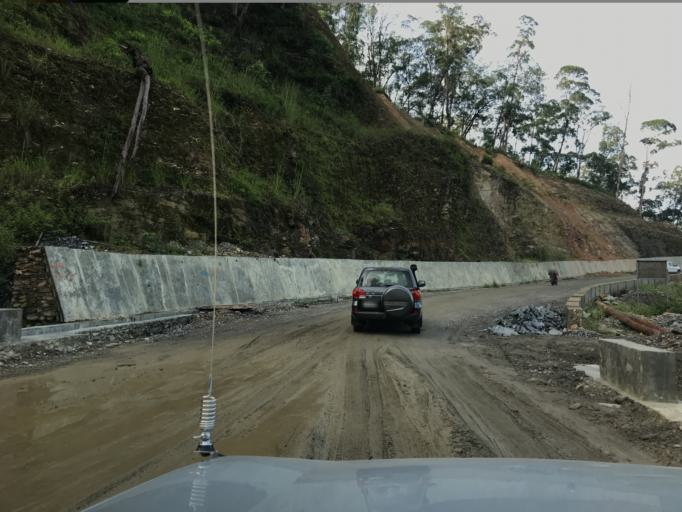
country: TL
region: Aileu
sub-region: Aileu Villa
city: Aileu
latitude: -8.6599
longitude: 125.5327
